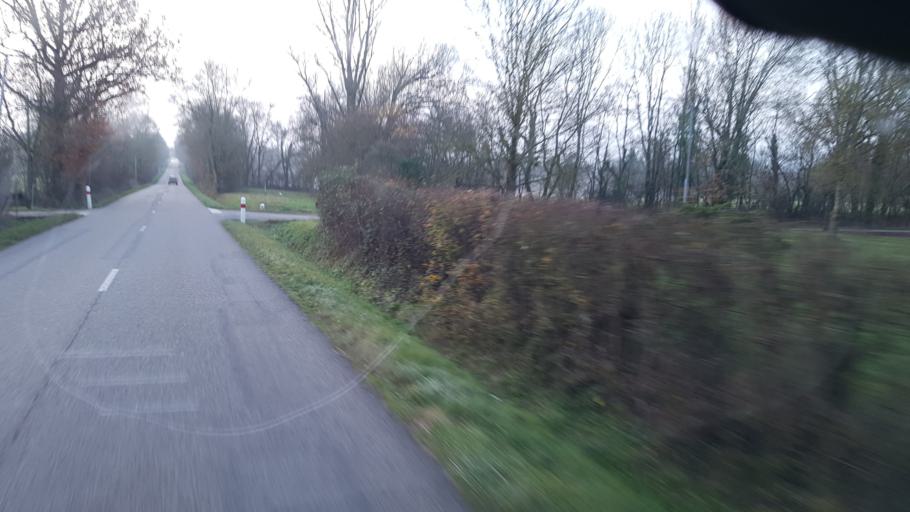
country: FR
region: Midi-Pyrenees
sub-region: Departement du Tarn-et-Garonne
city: Montricoux
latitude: 44.1050
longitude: 1.5982
